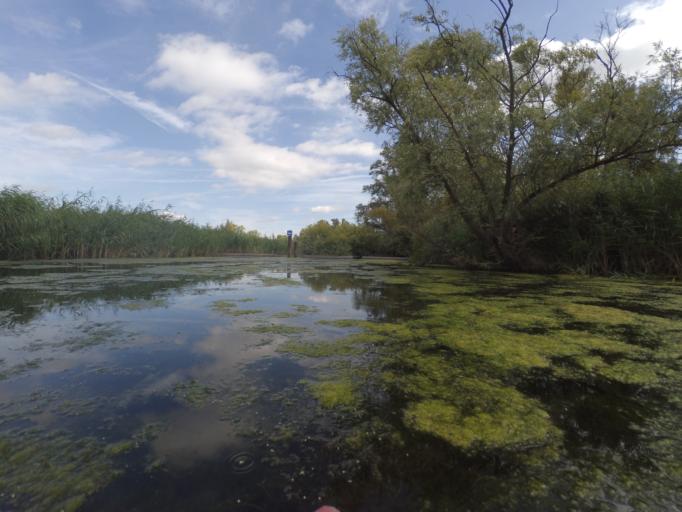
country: NL
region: North Brabant
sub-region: Gemeente Made en Drimmelen
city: Drimmelen
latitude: 51.7445
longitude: 4.7883
